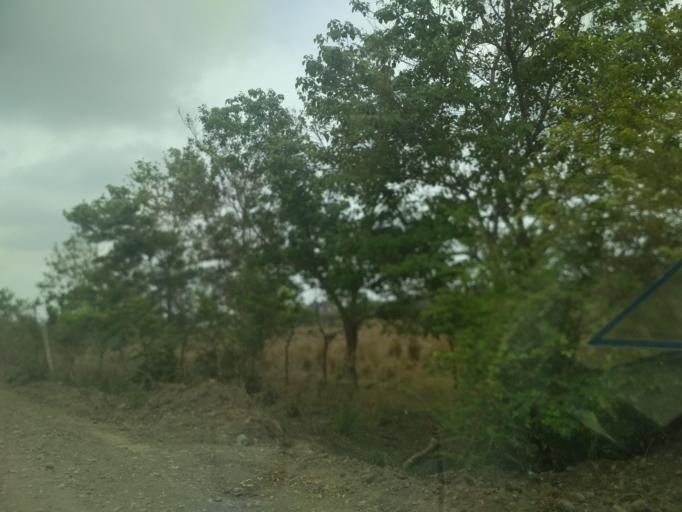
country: MX
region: Veracruz
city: Paso del Toro
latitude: 19.0113
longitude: -96.1334
